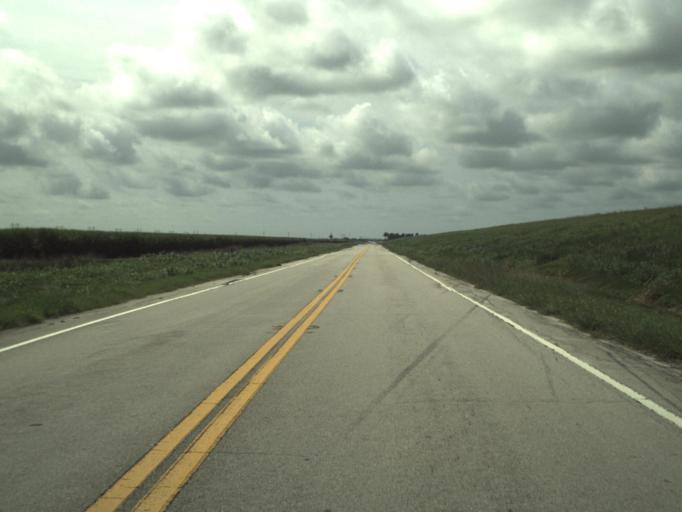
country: US
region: Florida
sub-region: Palm Beach County
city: Pahokee
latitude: 26.7662
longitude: -80.6887
